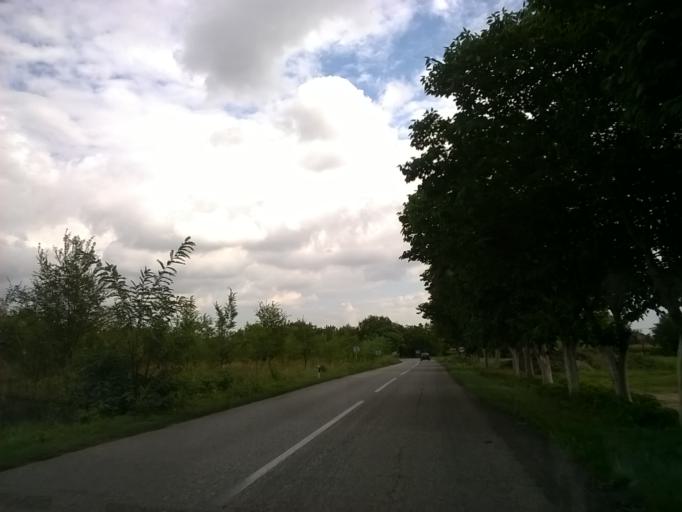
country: RS
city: Padina
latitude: 45.1181
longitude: 20.7134
